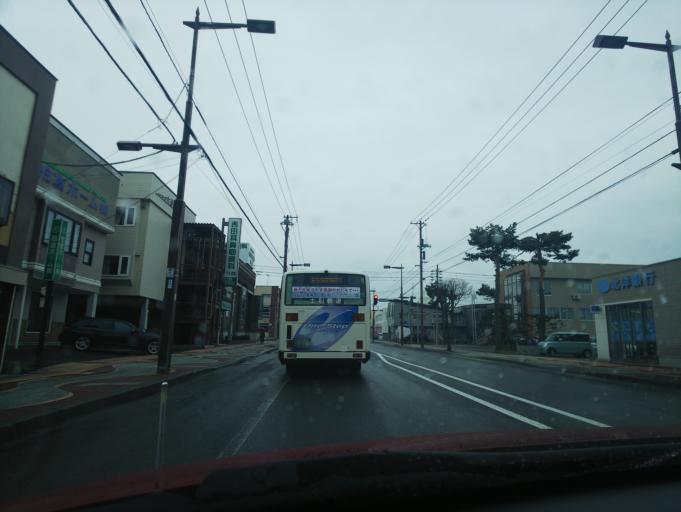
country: JP
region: Hokkaido
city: Nayoro
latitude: 44.1714
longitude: 142.3937
